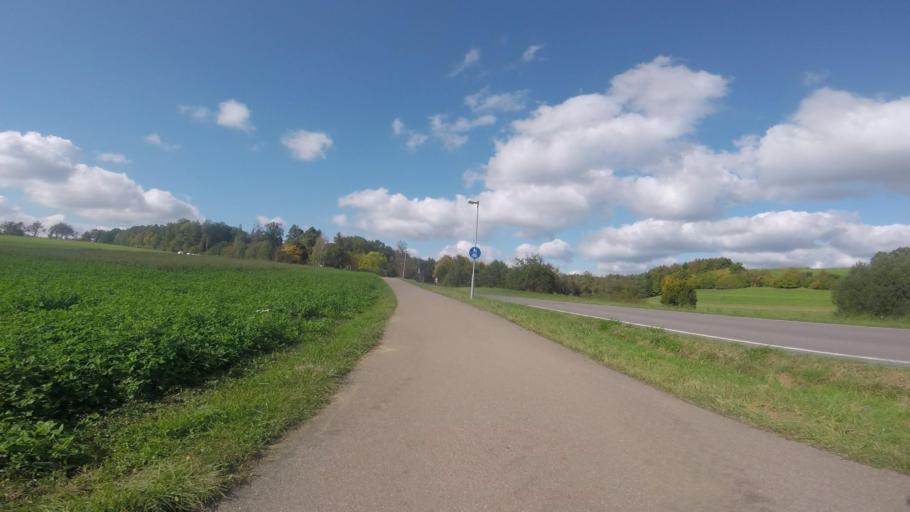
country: DE
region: Baden-Wuerttemberg
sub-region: Regierungsbezirk Stuttgart
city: Aspach
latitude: 48.9755
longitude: 9.3980
